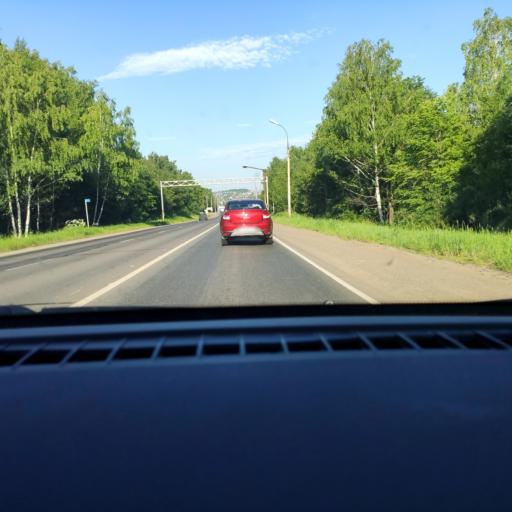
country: RU
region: Udmurtiya
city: Khokhryaki
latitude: 56.9145
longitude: 53.4020
